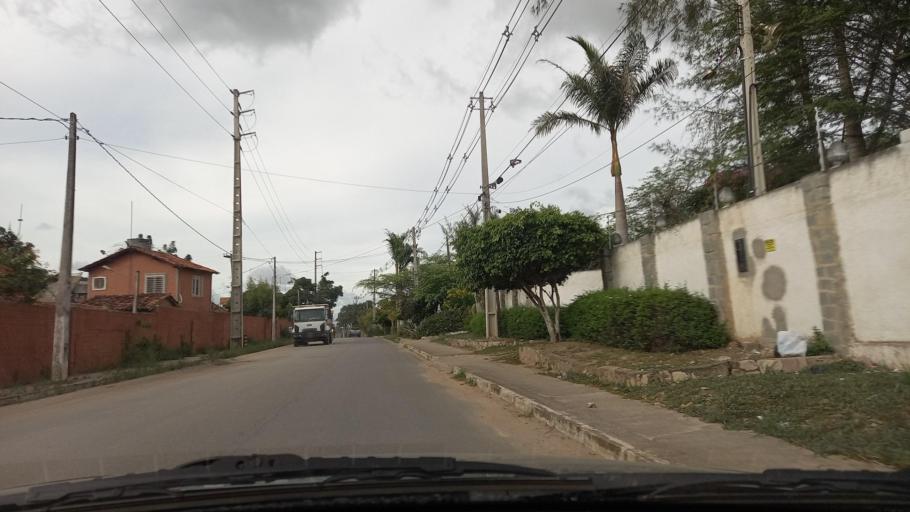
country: BR
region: Pernambuco
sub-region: Gravata
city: Gravata
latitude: -8.1993
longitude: -35.5429
